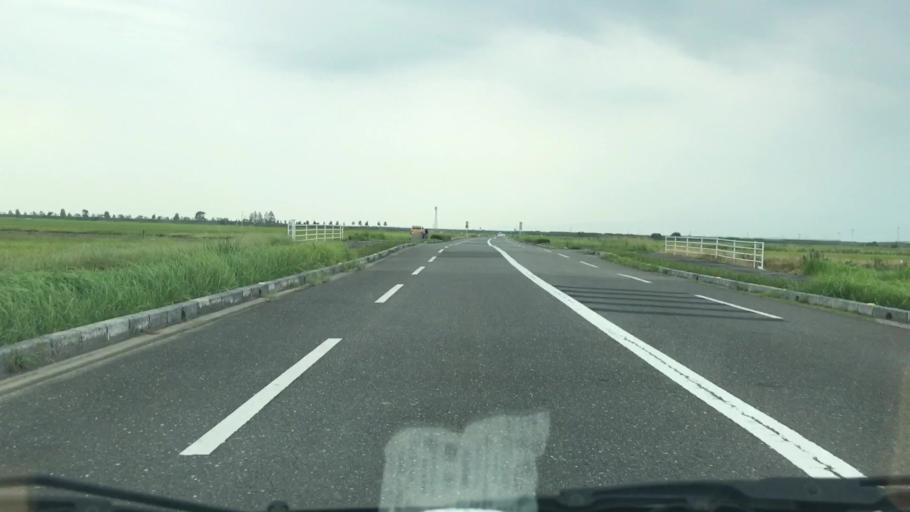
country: JP
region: Saga Prefecture
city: Okawa
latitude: 33.1669
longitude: 130.2929
